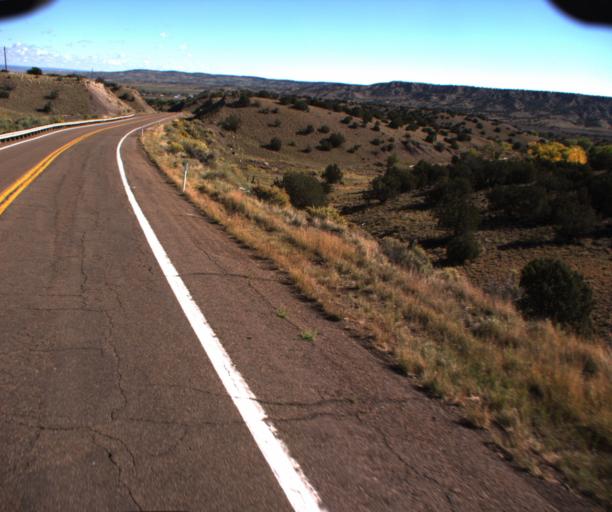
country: US
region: Arizona
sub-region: Apache County
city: Saint Johns
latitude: 34.4588
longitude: -109.6219
